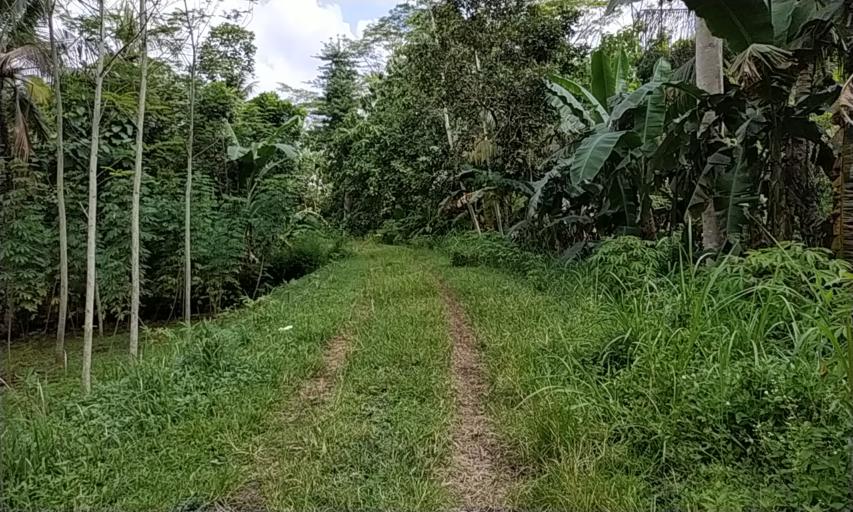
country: ID
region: Central Java
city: Bakung
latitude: -7.3498
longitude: 108.6601
